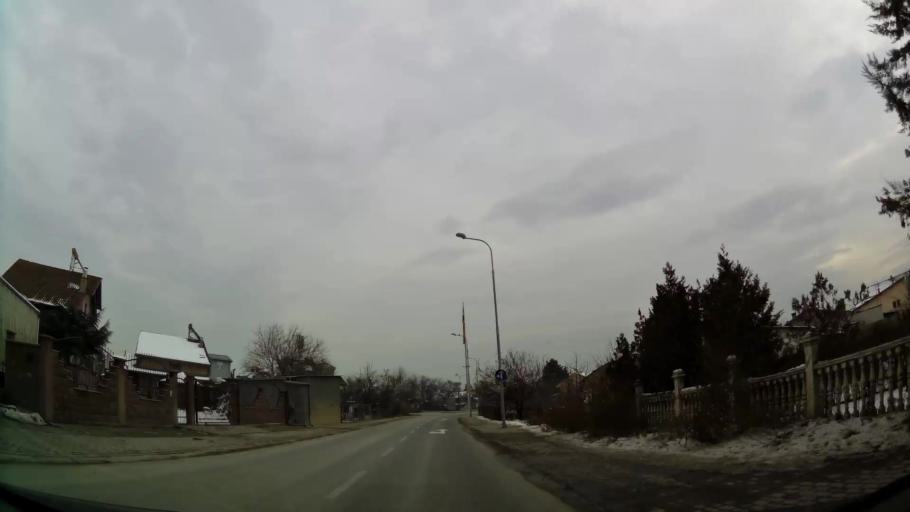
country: MK
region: Butel
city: Butel
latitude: 42.0356
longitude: 21.4450
